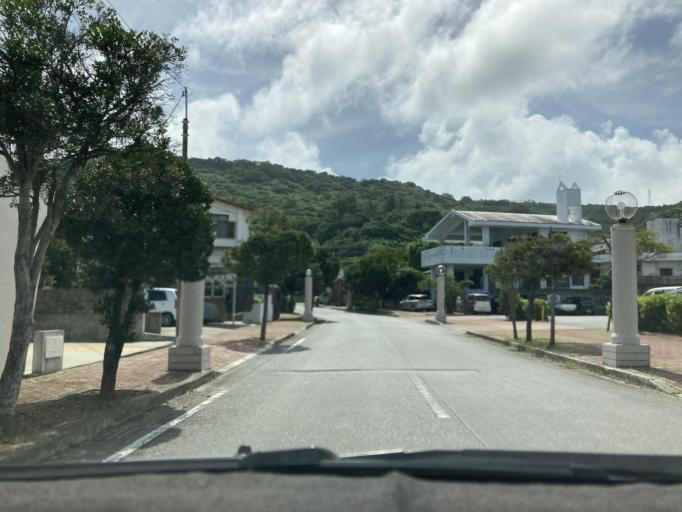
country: JP
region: Okinawa
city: Ginowan
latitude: 26.1687
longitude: 127.7880
